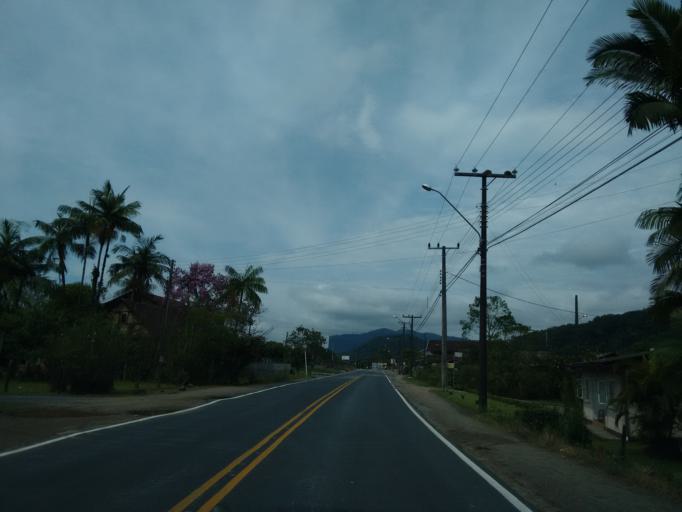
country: BR
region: Santa Catarina
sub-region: Pomerode
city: Pomerode
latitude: -26.6928
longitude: -49.1574
